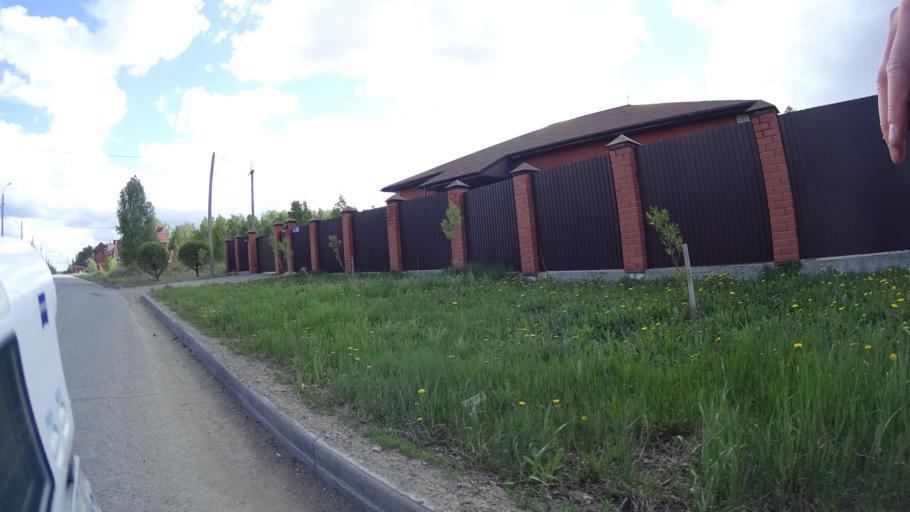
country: RU
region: Chelyabinsk
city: Sargazy
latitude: 55.1614
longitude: 61.2518
